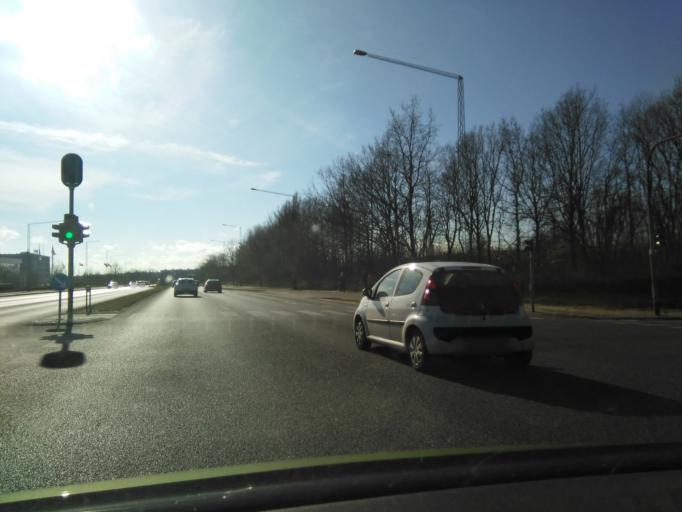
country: DK
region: Central Jutland
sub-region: Arhus Kommune
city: Stavtrup
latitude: 56.1694
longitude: 10.1538
